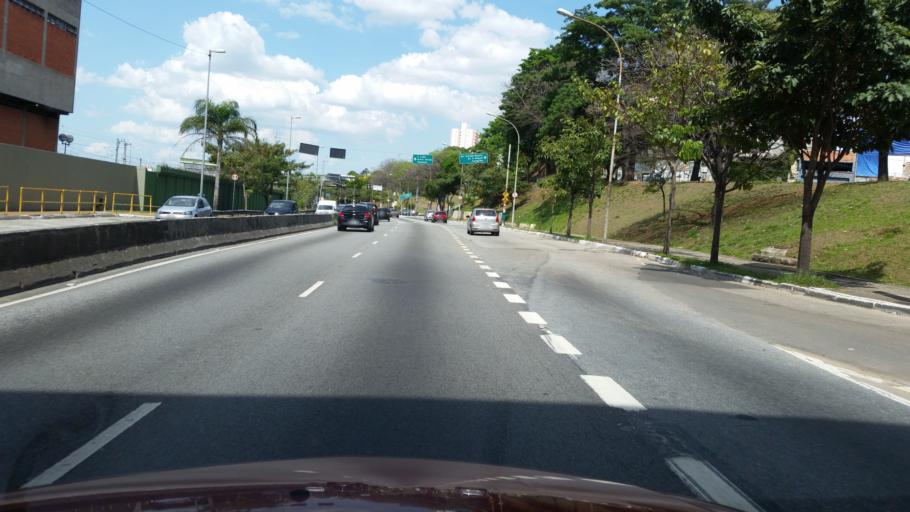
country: BR
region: Sao Paulo
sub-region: Guarulhos
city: Guarulhos
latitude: -23.5321
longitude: -46.5306
